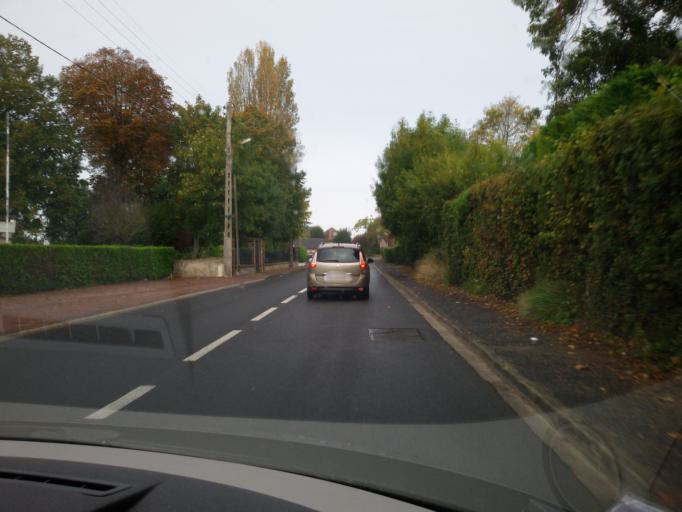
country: FR
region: Lower Normandy
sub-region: Departement du Calvados
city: Houlgate
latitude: 49.2994
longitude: -0.0700
